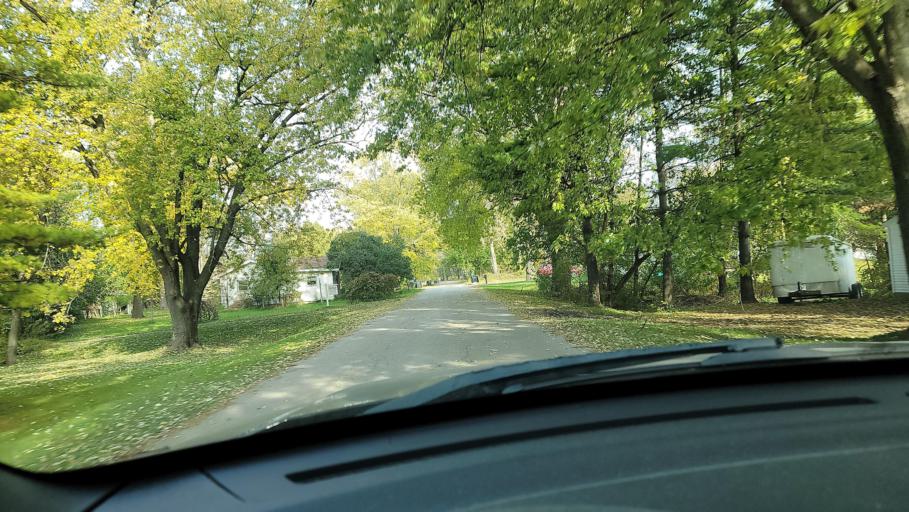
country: US
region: Indiana
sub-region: Porter County
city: Ogden Dunes
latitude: 41.6093
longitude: -87.1724
